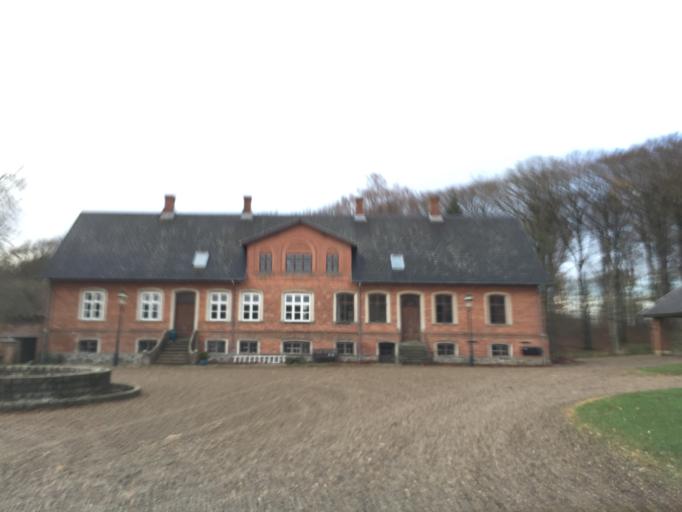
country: DK
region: Central Jutland
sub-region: Viborg Kommune
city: Bjerringbro
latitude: 56.2555
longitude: 9.6802
